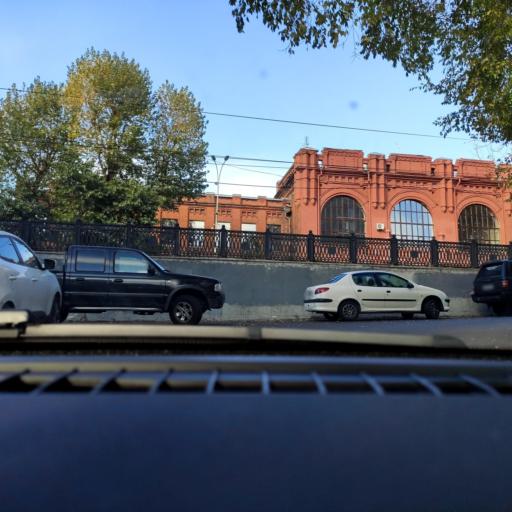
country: RU
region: Voronezj
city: Voronezh
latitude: 51.6789
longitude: 39.2147
